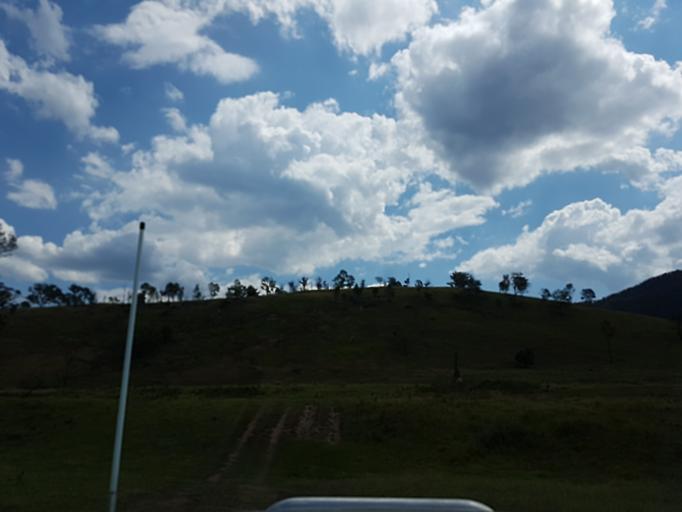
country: AU
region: Victoria
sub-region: East Gippsland
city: Lakes Entrance
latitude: -37.3972
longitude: 148.3341
